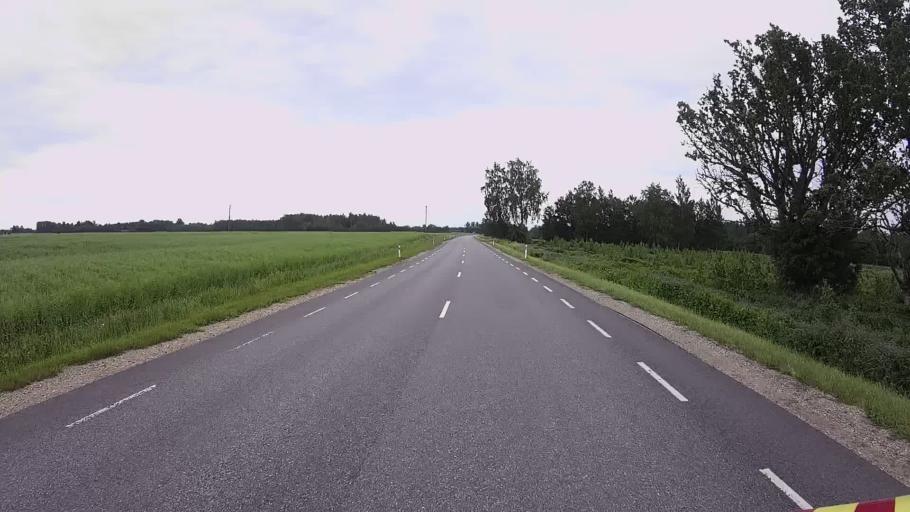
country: EE
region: Viljandimaa
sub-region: Karksi vald
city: Karksi-Nuia
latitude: 58.1677
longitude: 25.5809
